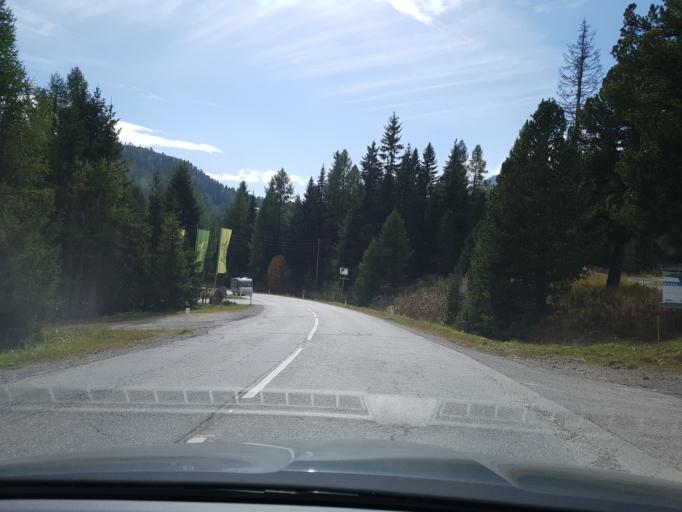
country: AT
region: Carinthia
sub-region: Politischer Bezirk Spittal an der Drau
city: Kleinkirchheim
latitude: 46.9329
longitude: 13.8709
